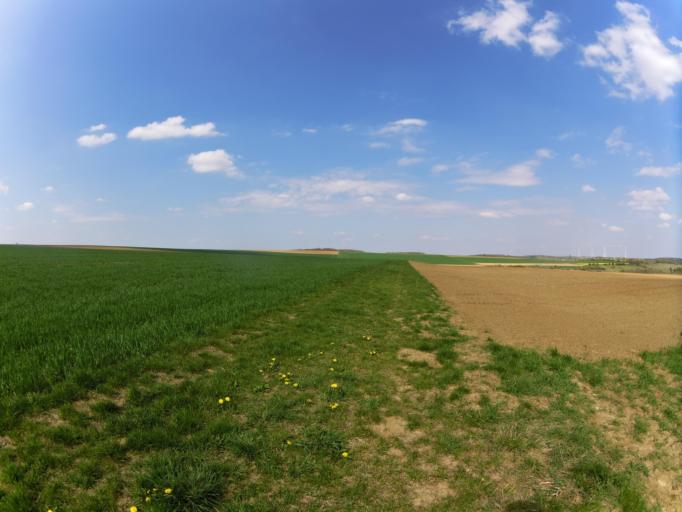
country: DE
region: Bavaria
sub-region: Regierungsbezirk Unterfranken
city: Winterhausen
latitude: 49.6831
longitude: 10.0060
